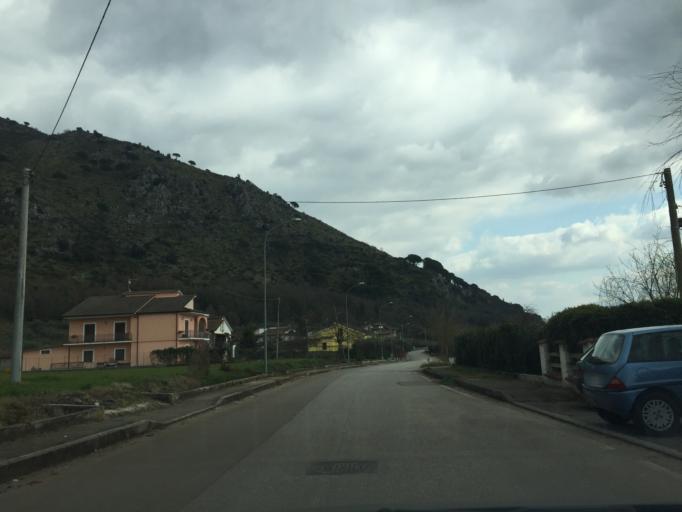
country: IT
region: Latium
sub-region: Provincia di Frosinone
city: Villa Santa Lucia
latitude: 41.4939
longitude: 13.7782
